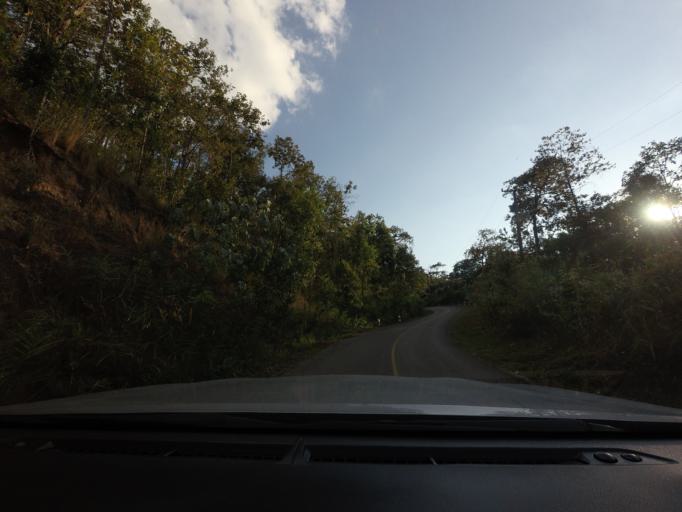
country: TH
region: Chiang Mai
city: Phrao
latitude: 19.4864
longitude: 99.1670
